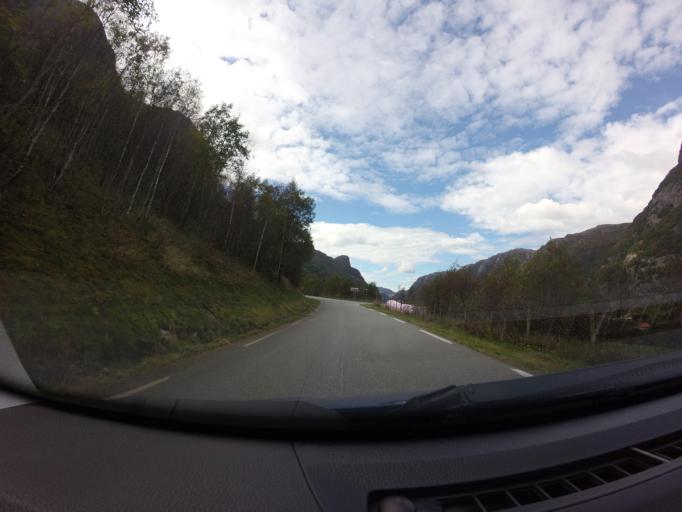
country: NO
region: Rogaland
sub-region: Forsand
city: Forsand
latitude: 58.8410
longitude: 6.2903
